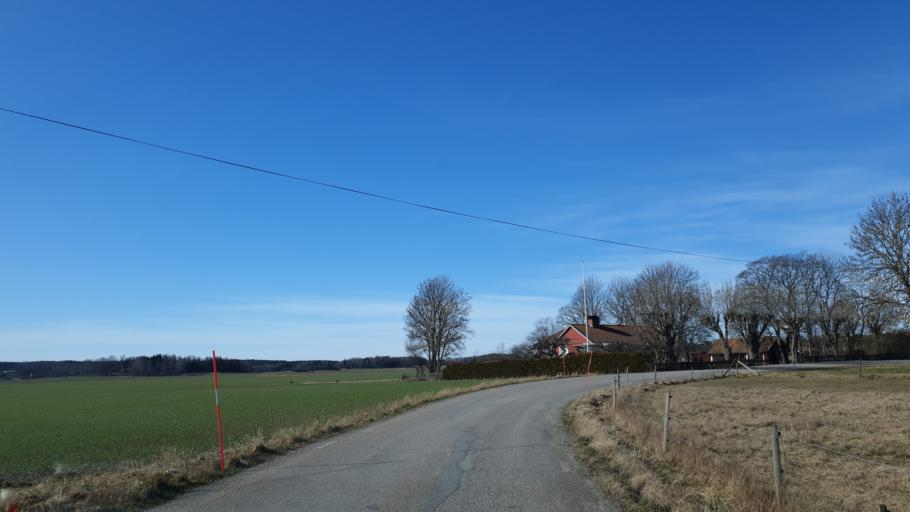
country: SE
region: Uppsala
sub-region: Enkopings Kommun
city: Dalby
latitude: 59.5176
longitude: 17.2836
